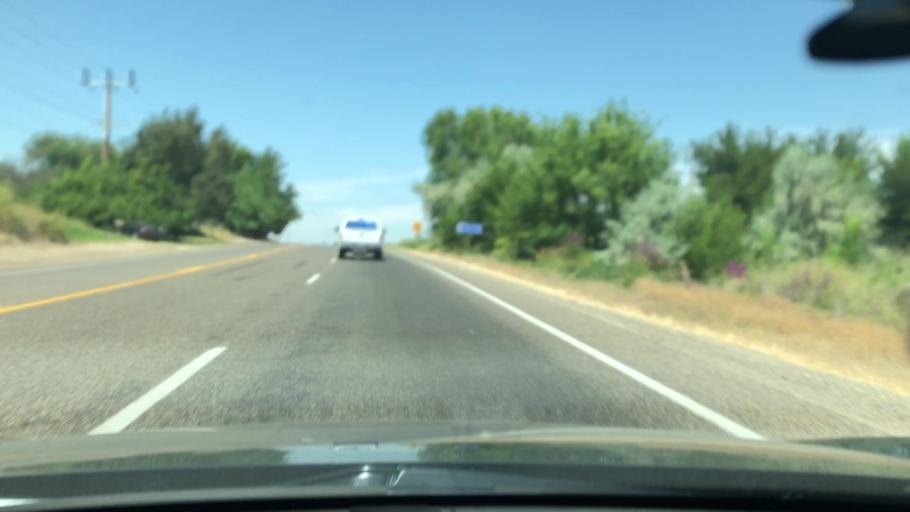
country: US
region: Idaho
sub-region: Canyon County
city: Wilder
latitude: 43.6597
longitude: -116.9117
